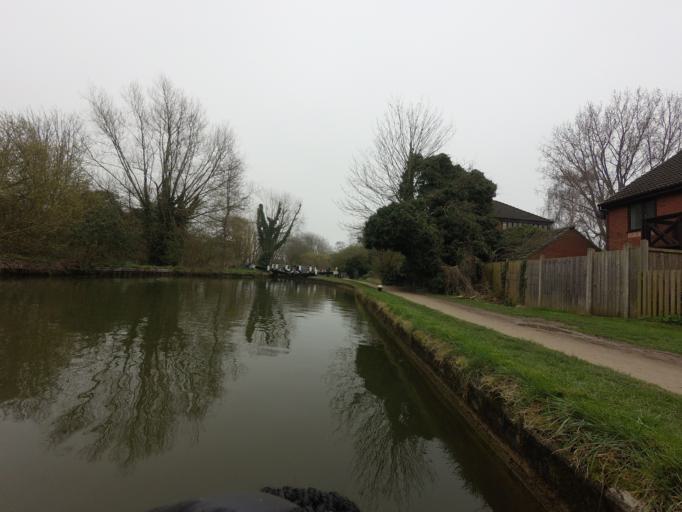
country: GB
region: England
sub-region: Hertfordshire
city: Berkhamsted
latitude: 51.7652
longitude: -0.5730
